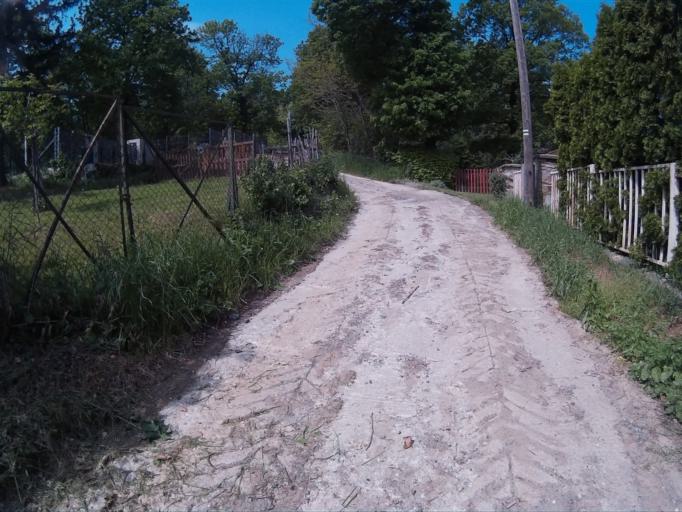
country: HU
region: Vas
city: Koszeg
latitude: 47.3765
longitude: 16.5244
